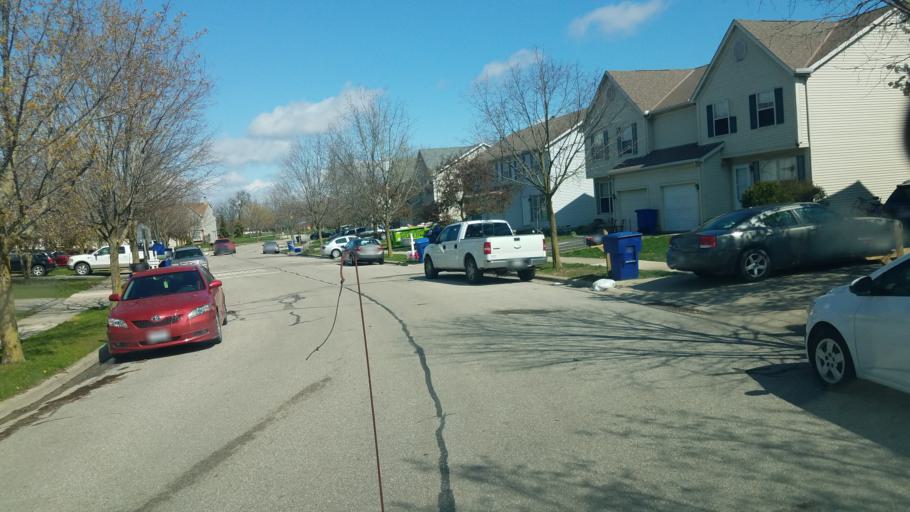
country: US
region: Ohio
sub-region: Delaware County
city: Delaware
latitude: 40.2989
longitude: -83.0940
